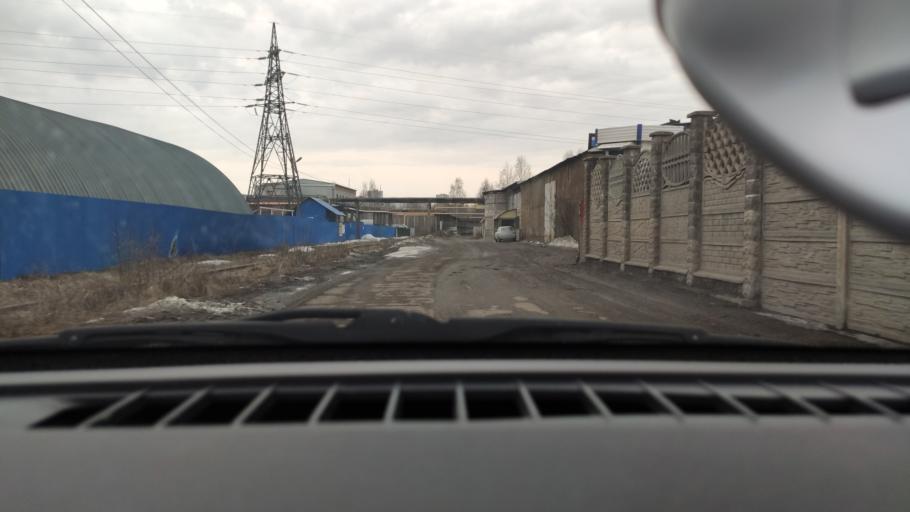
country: RU
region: Perm
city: Perm
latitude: 58.0434
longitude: 56.3124
